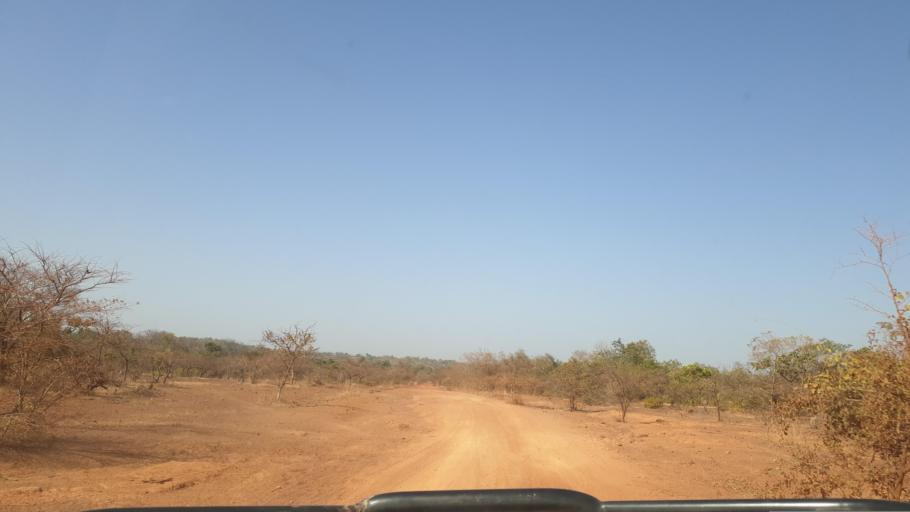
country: ML
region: Sikasso
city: Bougouni
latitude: 11.8209
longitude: -6.9599
